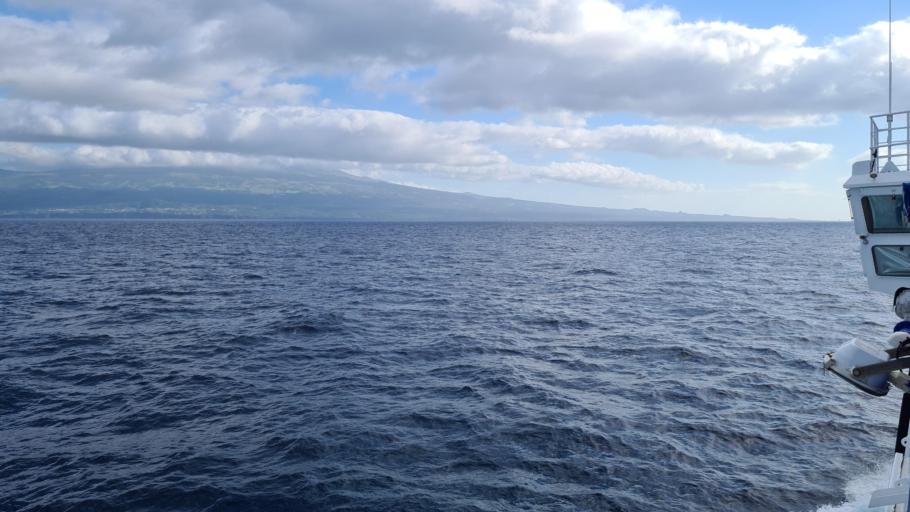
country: PT
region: Azores
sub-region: Sao Roque do Pico
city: Sao Roque do Pico
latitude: 38.6226
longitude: -28.3505
